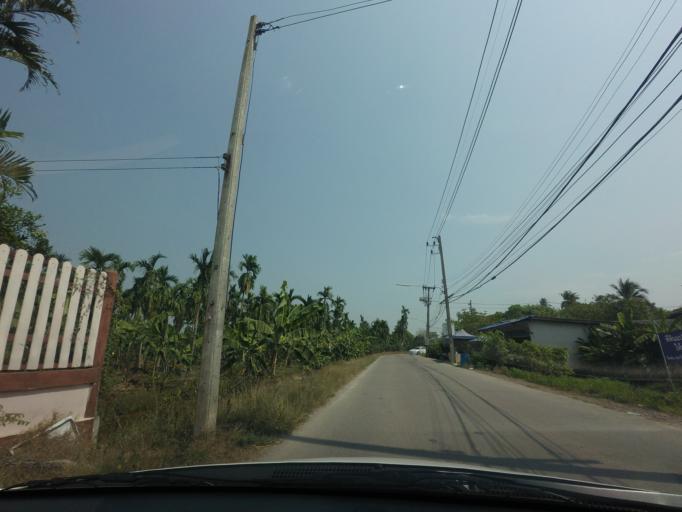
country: TH
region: Nakhon Pathom
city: Sam Phran
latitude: 13.7505
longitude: 100.2616
